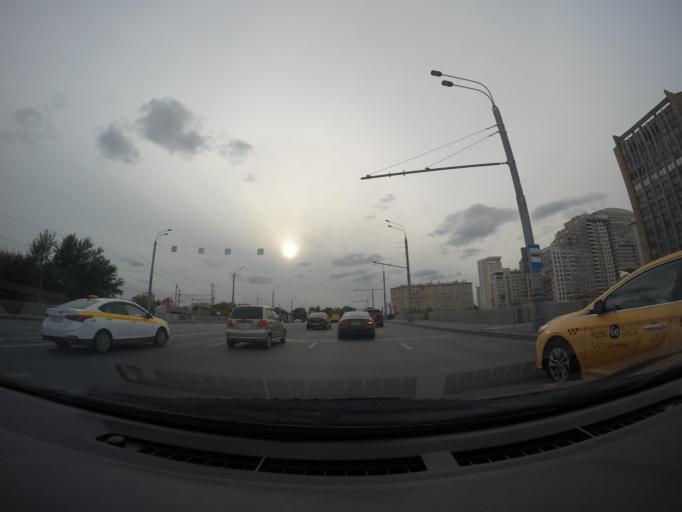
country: RU
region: Moscow
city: Lefortovo
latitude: 55.7828
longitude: 37.7010
